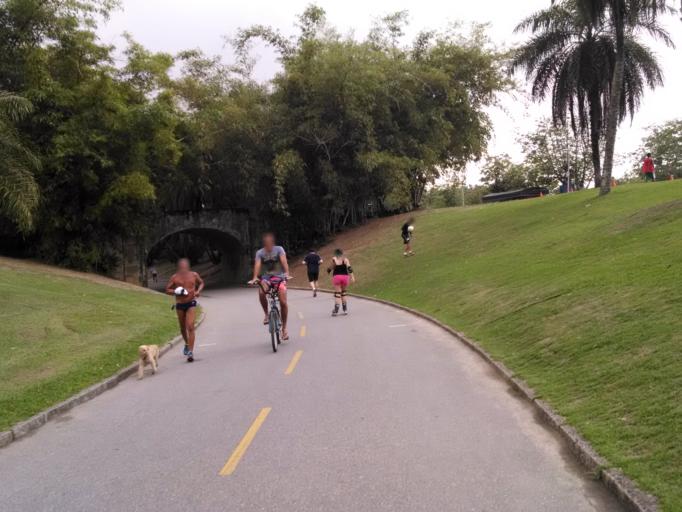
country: BR
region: Rio de Janeiro
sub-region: Rio De Janeiro
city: Rio de Janeiro
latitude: -22.9375
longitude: -43.1704
